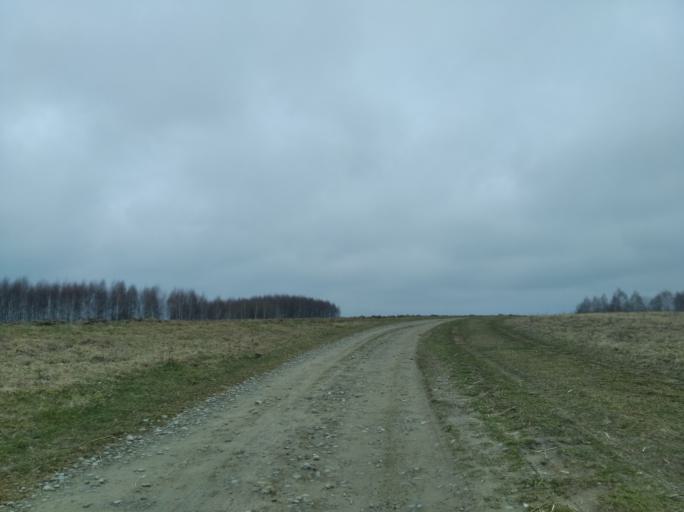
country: PL
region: Subcarpathian Voivodeship
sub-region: Powiat strzyzowski
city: Strzyzow
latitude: 49.8826
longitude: 21.8012
